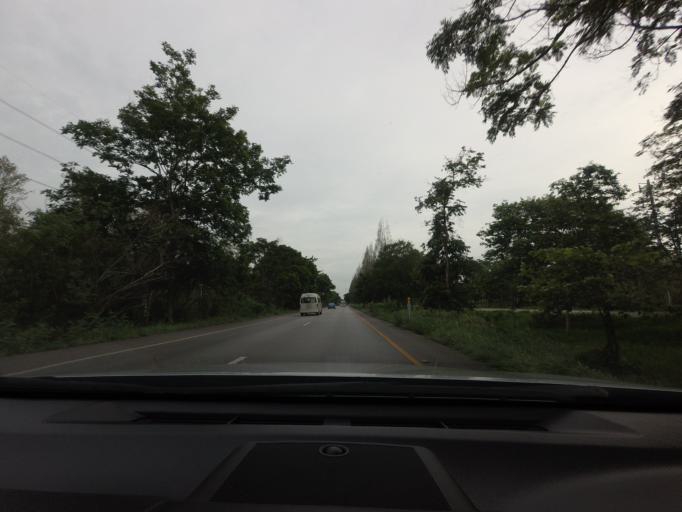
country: TH
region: Phetchaburi
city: Cha-am
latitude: 12.6980
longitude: 99.9060
